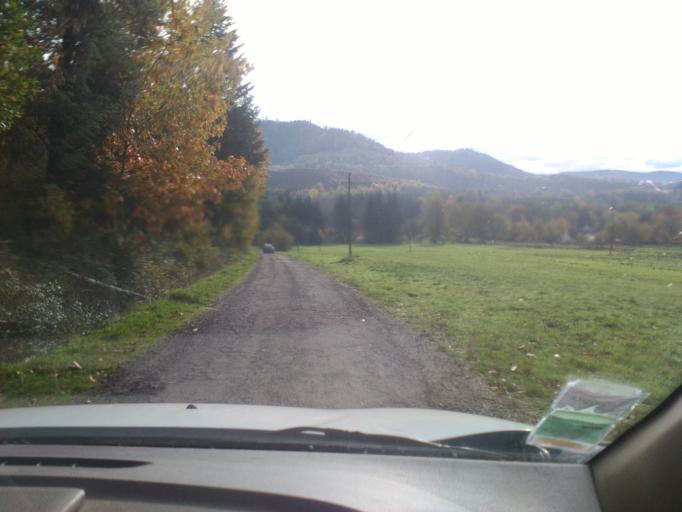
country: FR
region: Lorraine
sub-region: Departement des Vosges
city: Moyenmoutier
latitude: 48.4188
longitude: 6.8757
